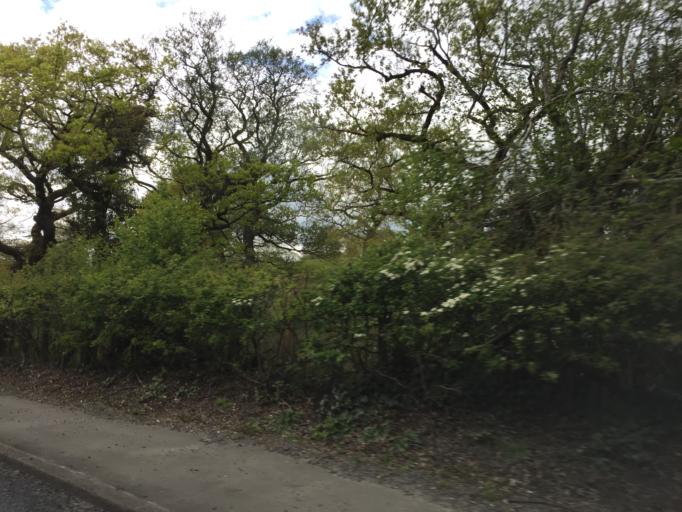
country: GB
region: Wales
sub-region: Caerphilly County Borough
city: Nelson
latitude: 51.6478
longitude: -3.2967
